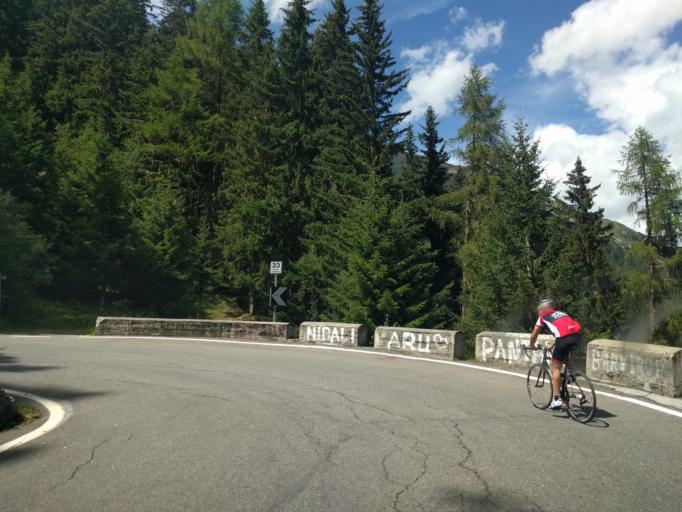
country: IT
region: Trentino-Alto Adige
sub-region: Bolzano
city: Stelvio
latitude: 46.5393
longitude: 10.5002
